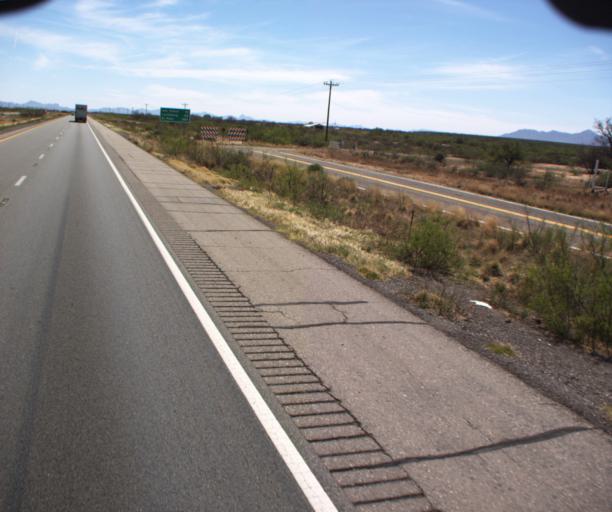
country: US
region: Arizona
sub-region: Cochise County
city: Willcox
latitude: 32.3116
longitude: -109.4172
